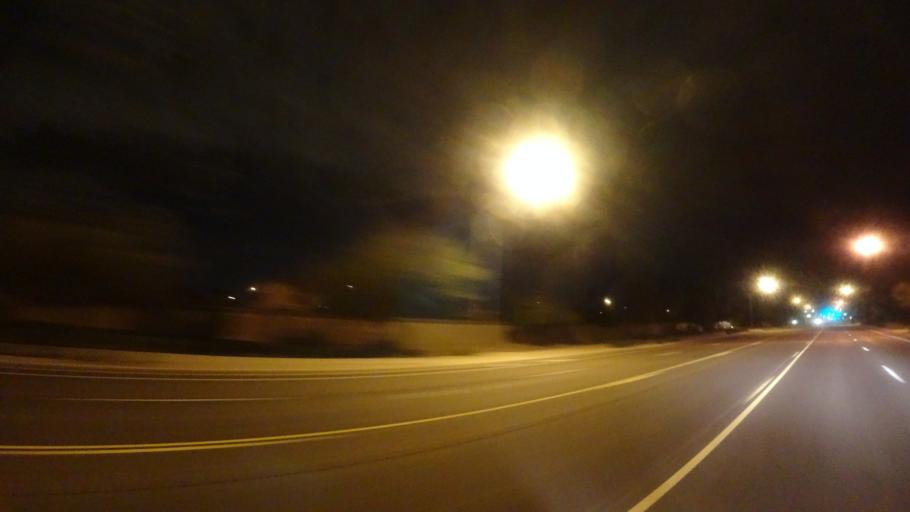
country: US
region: Arizona
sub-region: Maricopa County
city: Gilbert
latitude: 33.3609
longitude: -111.7046
